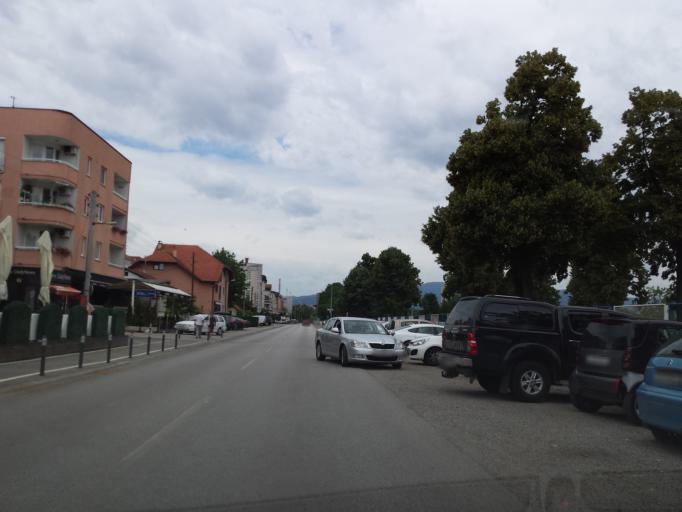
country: HR
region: Grad Zagreb
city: Novi Zagreb
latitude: 45.7817
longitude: 15.9666
